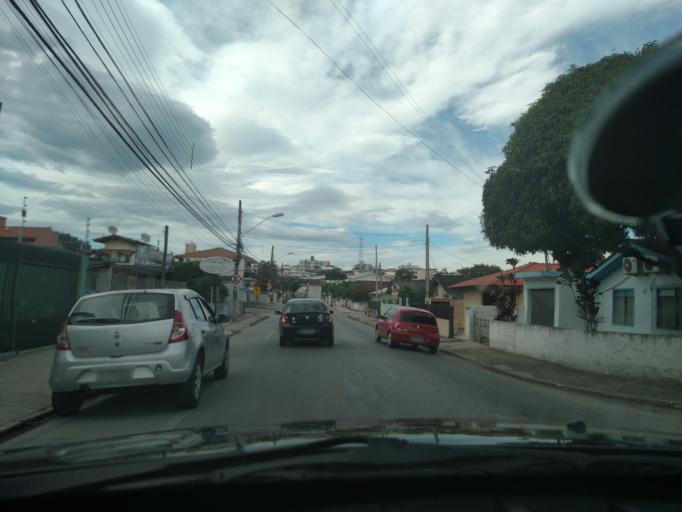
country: BR
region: Santa Catarina
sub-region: Sao Jose
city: Campinas
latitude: -27.6024
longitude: -48.6397
